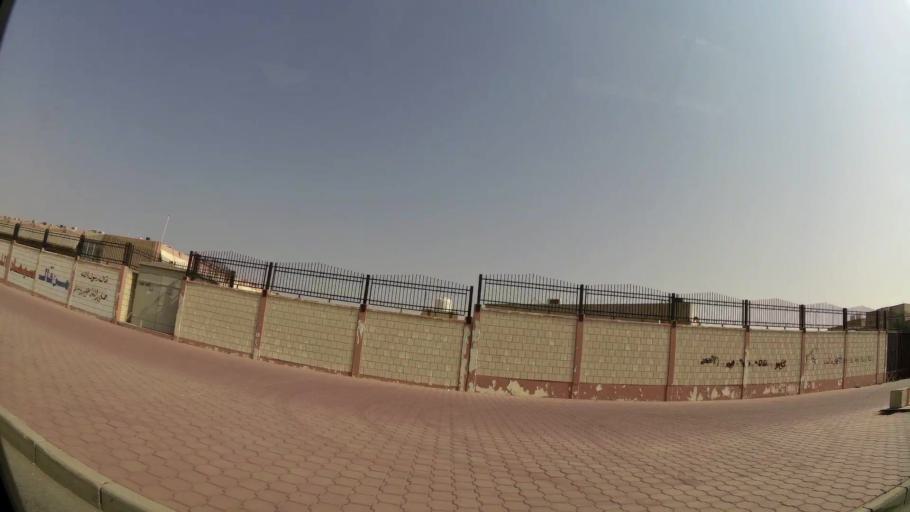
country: KW
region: Muhafazat al Jahra'
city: Al Jahra'
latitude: 29.3301
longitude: 47.6509
